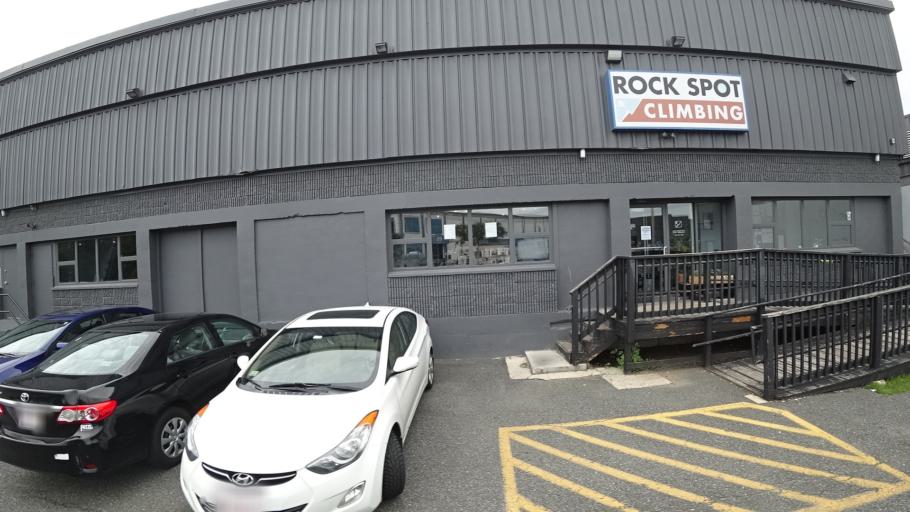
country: US
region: Massachusetts
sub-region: Norfolk County
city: Dedham
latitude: 42.2351
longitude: -71.1384
